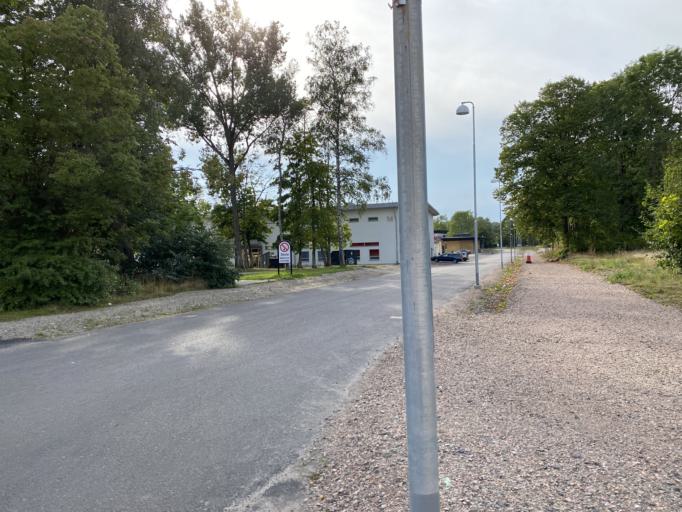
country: SE
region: Skane
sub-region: Lunds Kommun
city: Lund
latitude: 55.7037
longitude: 13.2252
